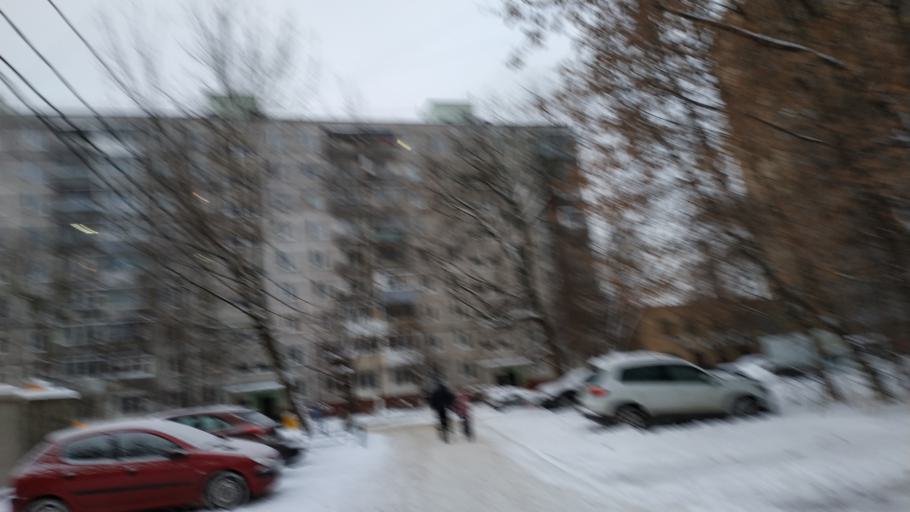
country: RU
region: Moskovskaya
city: Shchelkovo
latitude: 55.9277
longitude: 37.9913
